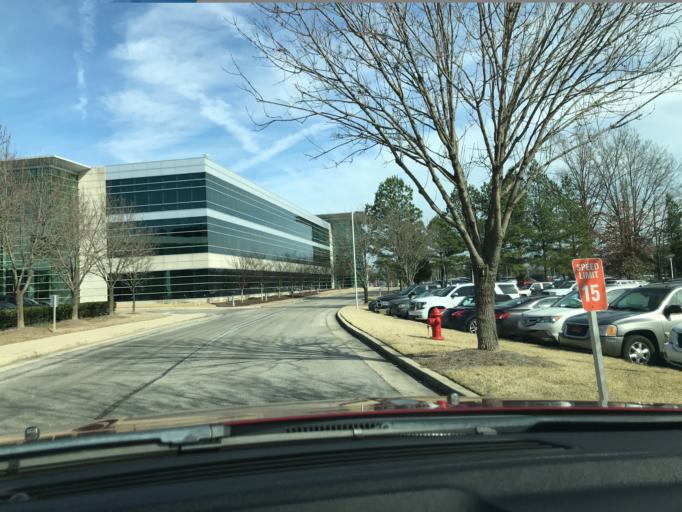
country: US
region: Tennessee
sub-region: Shelby County
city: Germantown
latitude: 35.0498
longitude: -89.7873
